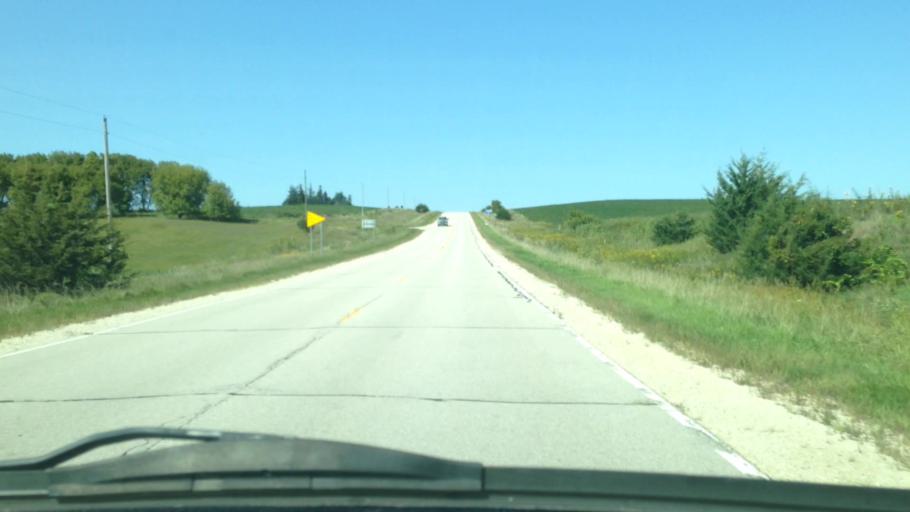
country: US
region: Minnesota
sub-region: Houston County
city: Spring Grove
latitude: 43.6327
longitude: -91.7903
